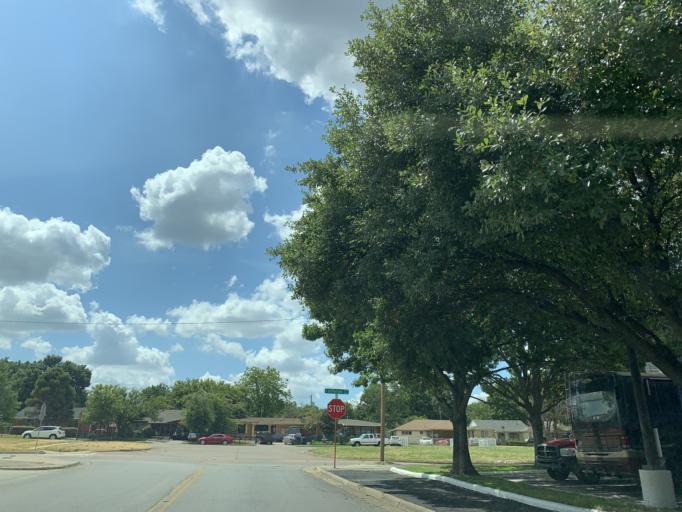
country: US
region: Texas
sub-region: Dallas County
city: Cockrell Hill
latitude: 32.7485
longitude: -96.8609
